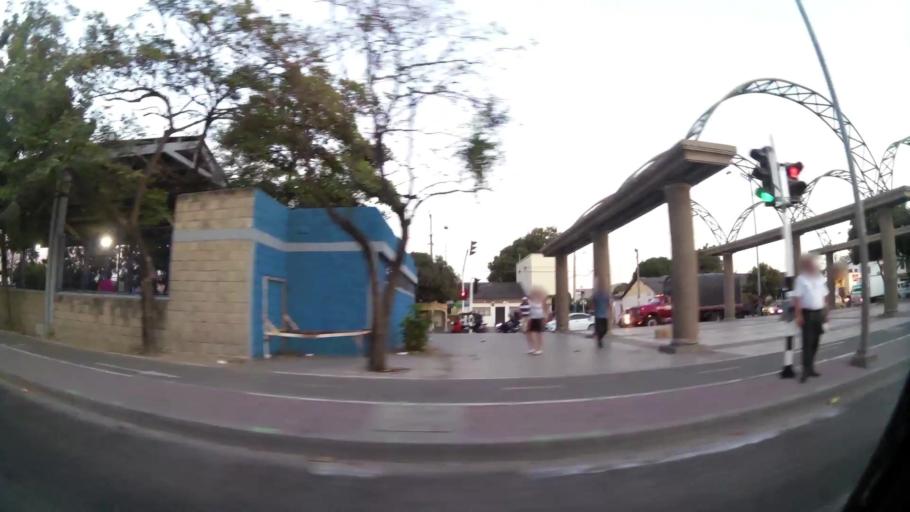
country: CO
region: Atlantico
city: Barranquilla
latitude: 10.9439
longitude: -74.7771
